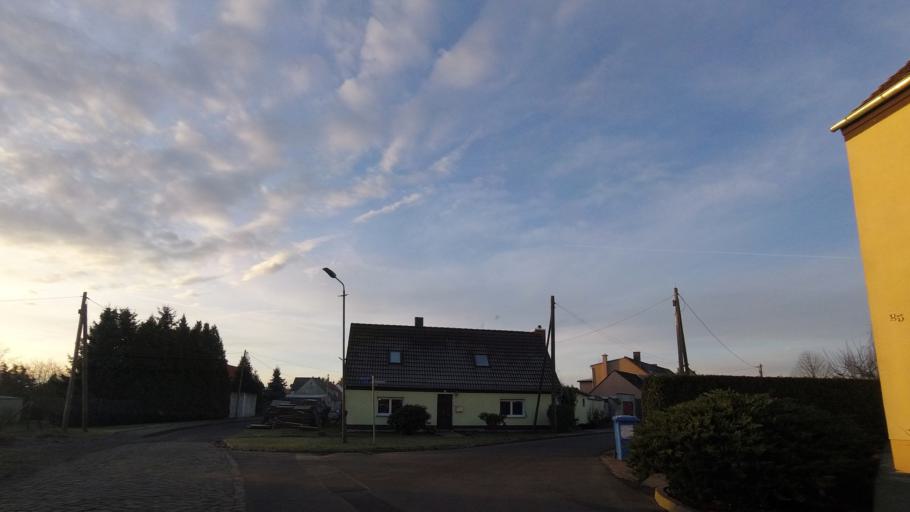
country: DE
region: Brandenburg
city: Niedergorsdorf
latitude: 51.9703
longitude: 12.9659
